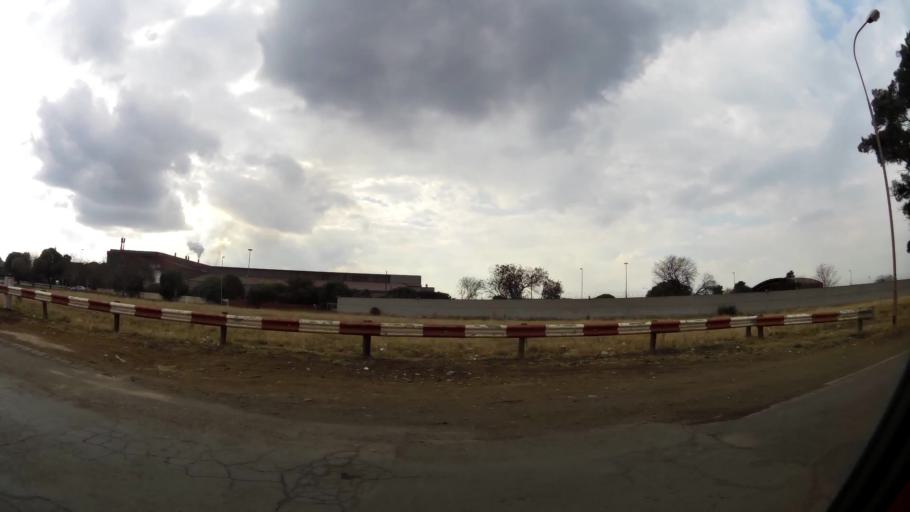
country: ZA
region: Gauteng
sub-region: Sedibeng District Municipality
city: Vanderbijlpark
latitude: -26.6726
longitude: 27.8192
